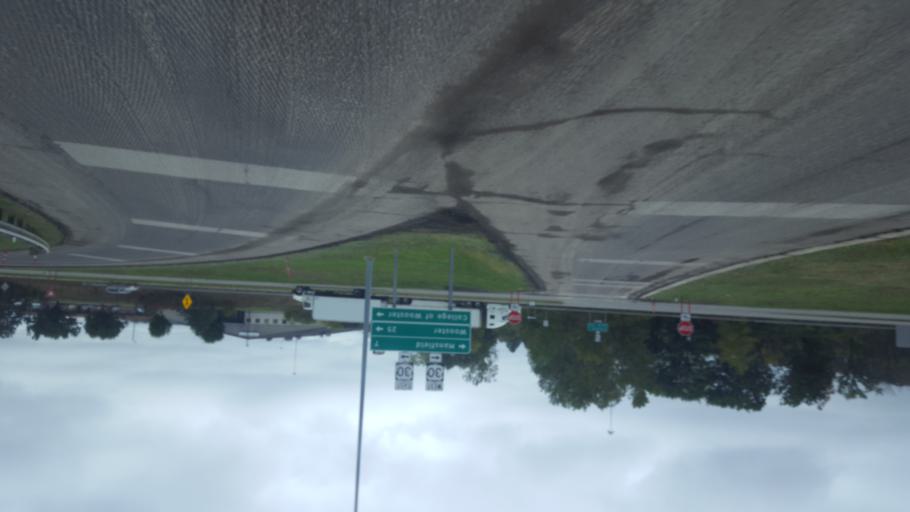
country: US
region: Ohio
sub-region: Richland County
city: Lincoln Heights
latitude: 40.7824
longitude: -82.4095
